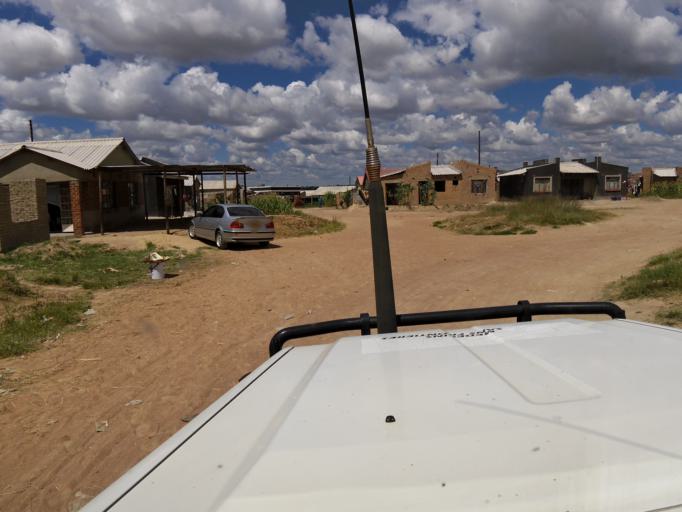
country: ZW
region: Harare
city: Epworth
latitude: -17.9218
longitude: 31.1429
